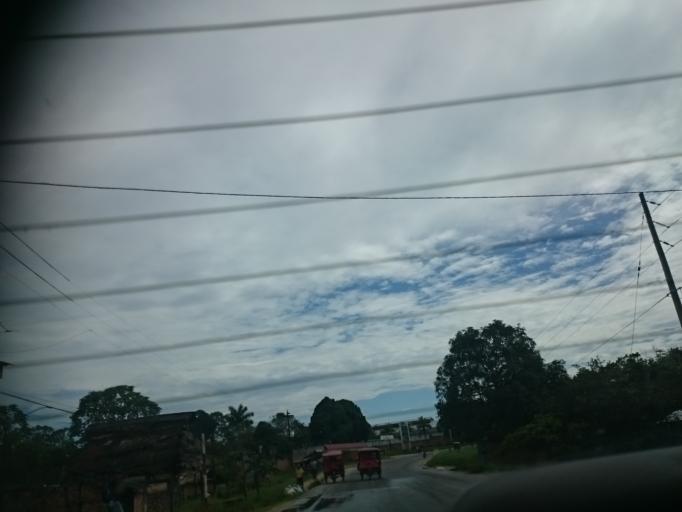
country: PE
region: Loreto
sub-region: Provincia de Maynas
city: Iquitos
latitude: -3.8220
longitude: -73.3256
